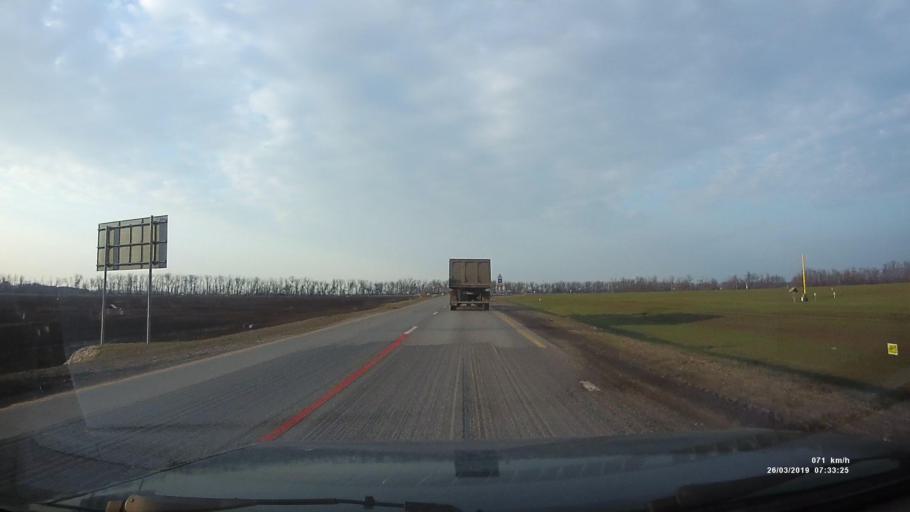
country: RU
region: Rostov
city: Novobessergenovka
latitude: 47.2153
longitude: 38.7703
